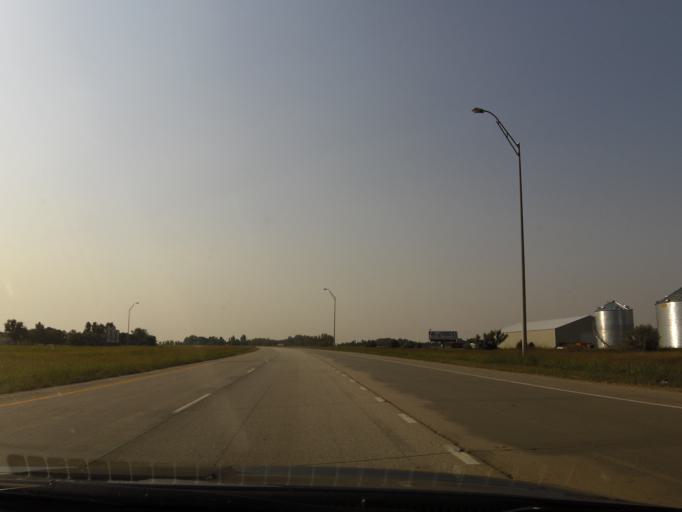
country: US
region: North Dakota
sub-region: Grand Forks County
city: Grand Forks
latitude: 48.0744
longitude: -97.1694
